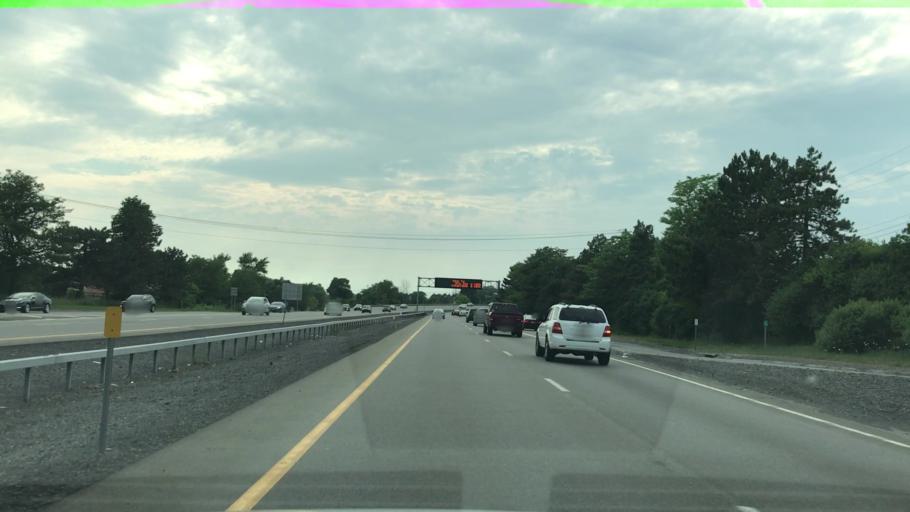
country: US
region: New York
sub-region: Erie County
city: Cheektowaga
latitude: 42.9302
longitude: -78.7562
